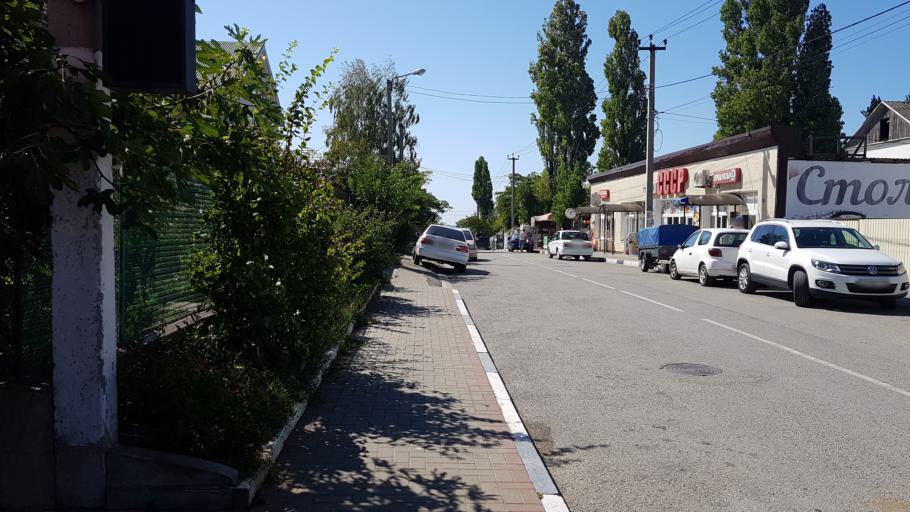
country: RU
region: Krasnodarskiy
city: Arkhipo-Osipovka
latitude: 44.3660
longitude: 38.5324
